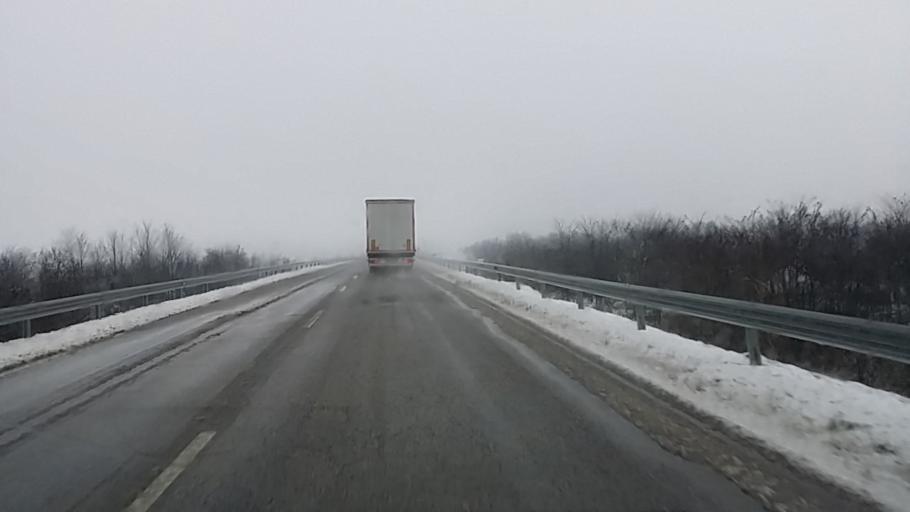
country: HU
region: Komarom-Esztergom
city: Komarom
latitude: 47.7410
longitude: 18.0928
